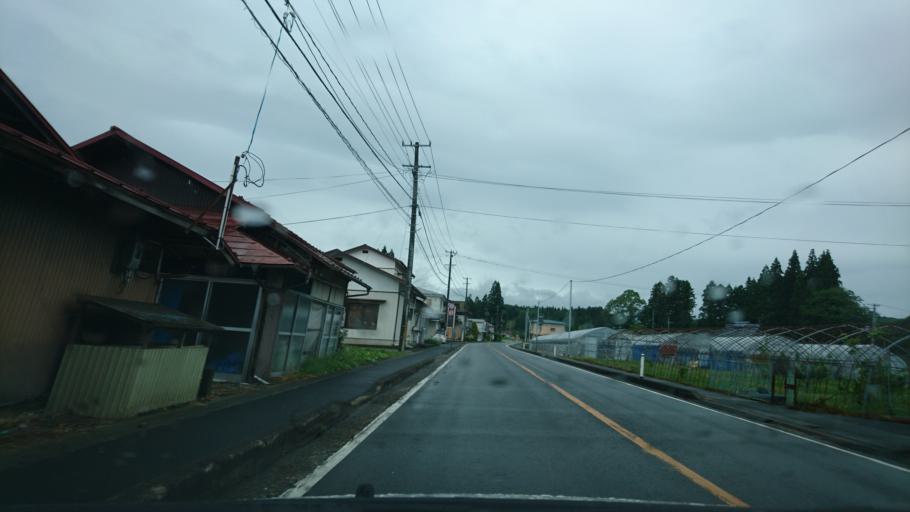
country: JP
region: Iwate
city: Ichinoseki
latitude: 38.9707
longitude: 140.9961
